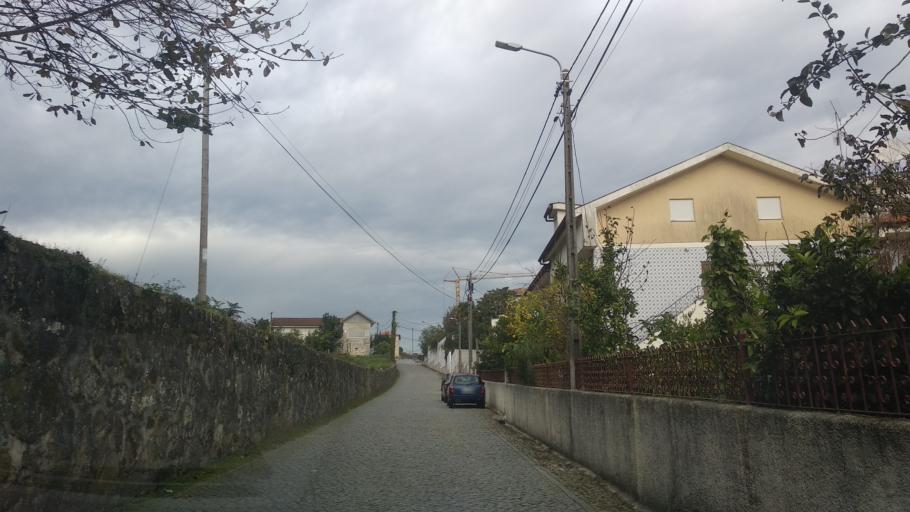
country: PT
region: Braga
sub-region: Braga
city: Braga
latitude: 41.5423
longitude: -8.4593
